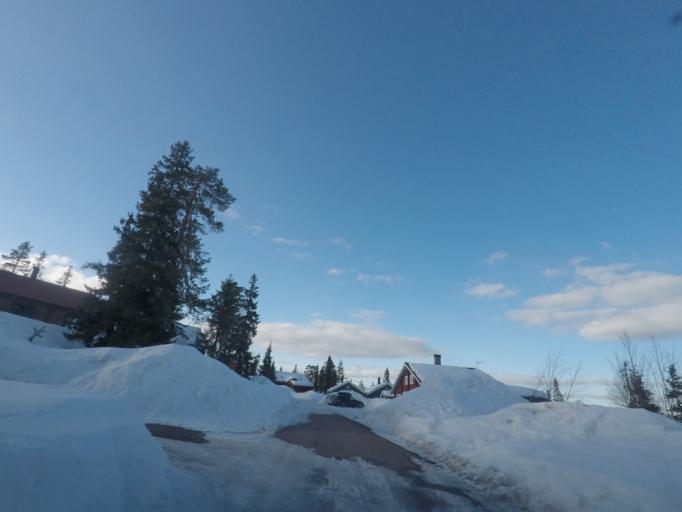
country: SE
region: Dalarna
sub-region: Malung-Saelens kommun
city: Malung
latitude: 61.1720
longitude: 13.1895
